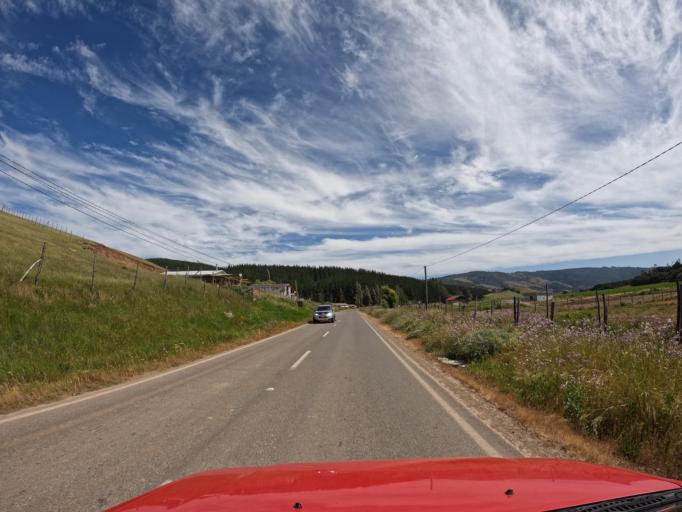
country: CL
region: Maule
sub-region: Provincia de Talca
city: Constitucion
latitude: -35.0330
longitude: -72.0533
